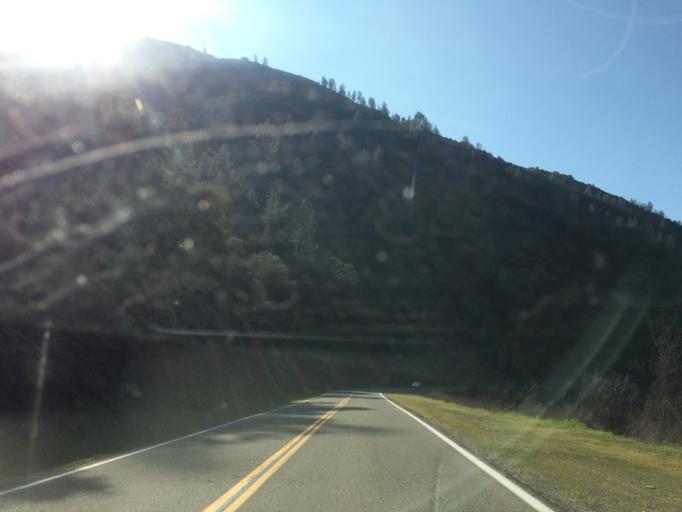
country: US
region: California
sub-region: Mariposa County
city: Midpines
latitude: 37.6144
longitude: -119.9574
